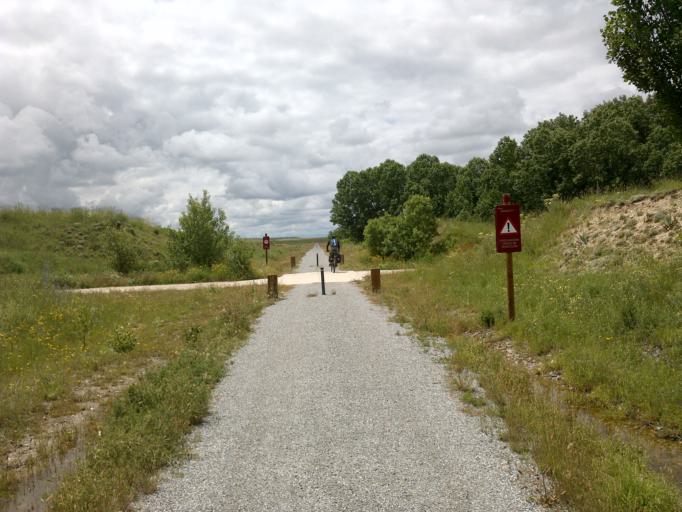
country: ES
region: Castille and Leon
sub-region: Provincia de Segovia
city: Armuna
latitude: 41.0858
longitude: -4.3510
